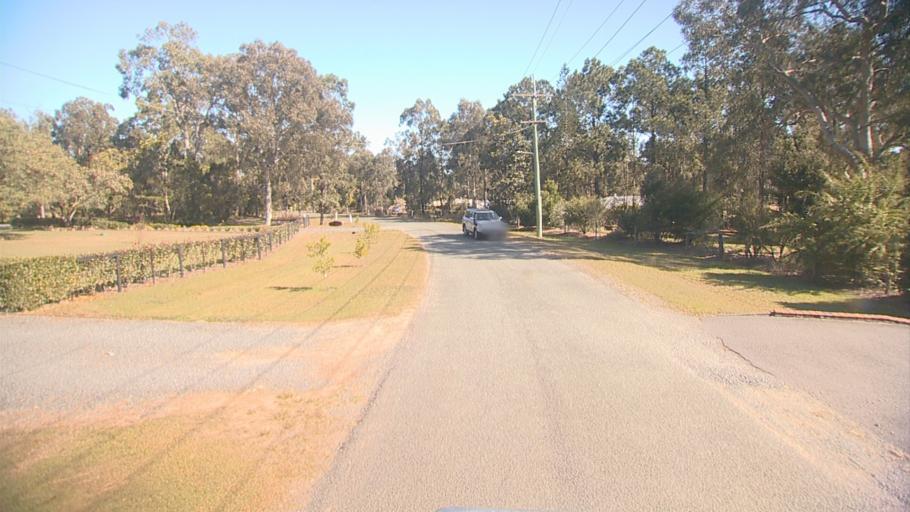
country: AU
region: Queensland
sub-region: Logan
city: Chambers Flat
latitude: -27.7768
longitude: 153.1076
